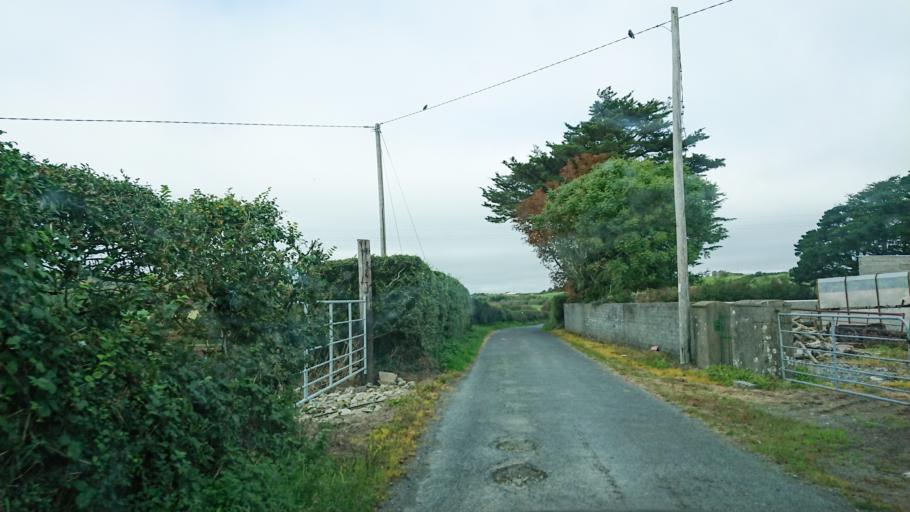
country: IE
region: Munster
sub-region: Waterford
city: Tra Mhor
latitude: 52.1927
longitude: -7.1234
